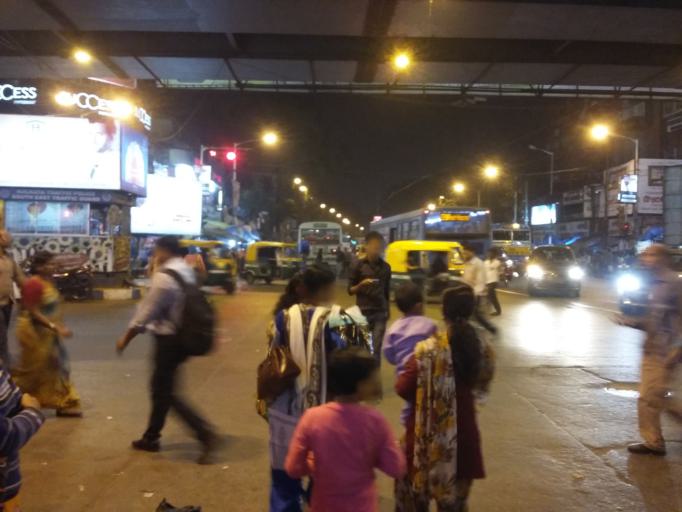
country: IN
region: West Bengal
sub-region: Kolkata
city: Kolkata
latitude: 22.5197
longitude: 88.3655
